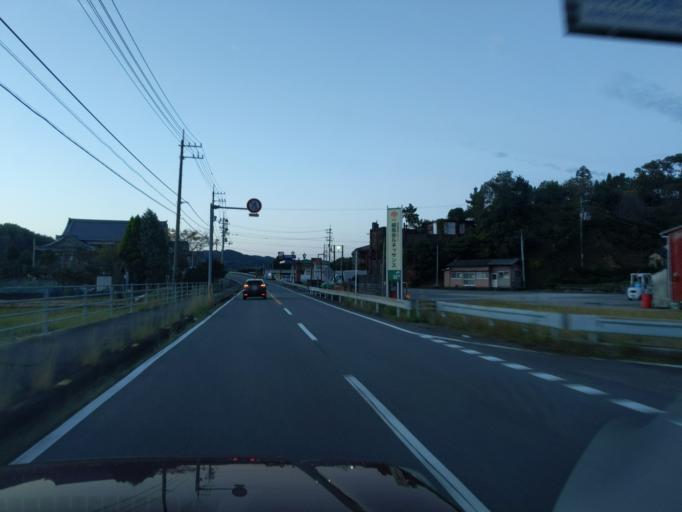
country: JP
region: Tokushima
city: Anan
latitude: 33.8515
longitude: 134.6263
